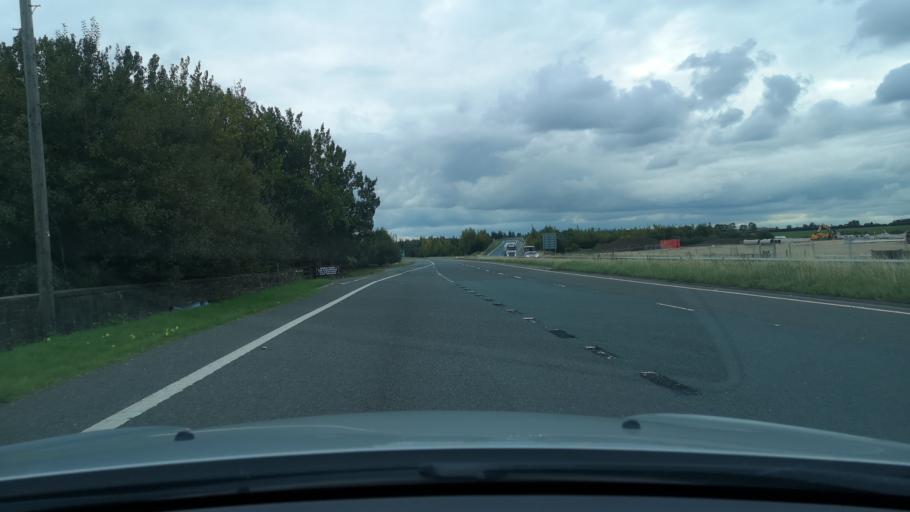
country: GB
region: England
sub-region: City and Borough of Wakefield
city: Darrington
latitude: 53.6899
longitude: -1.2658
